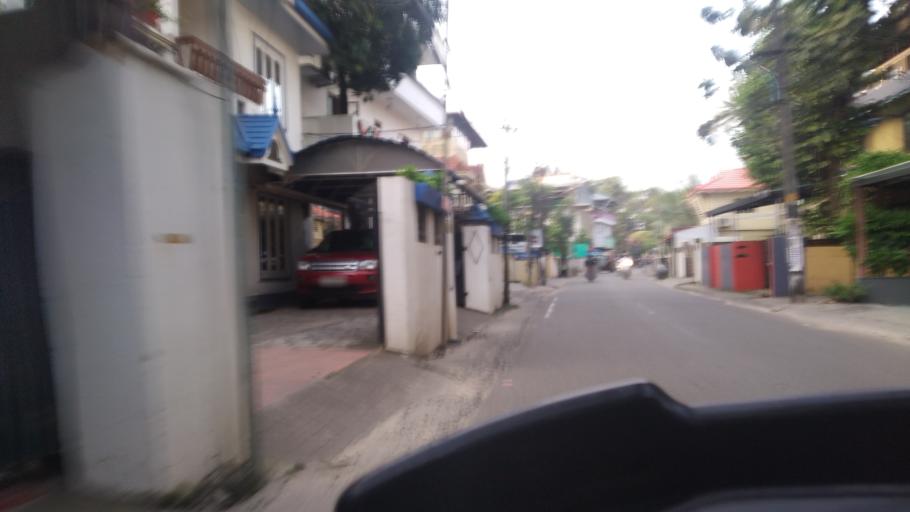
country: IN
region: Kerala
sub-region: Ernakulam
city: Elur
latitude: 10.0265
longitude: 76.2985
